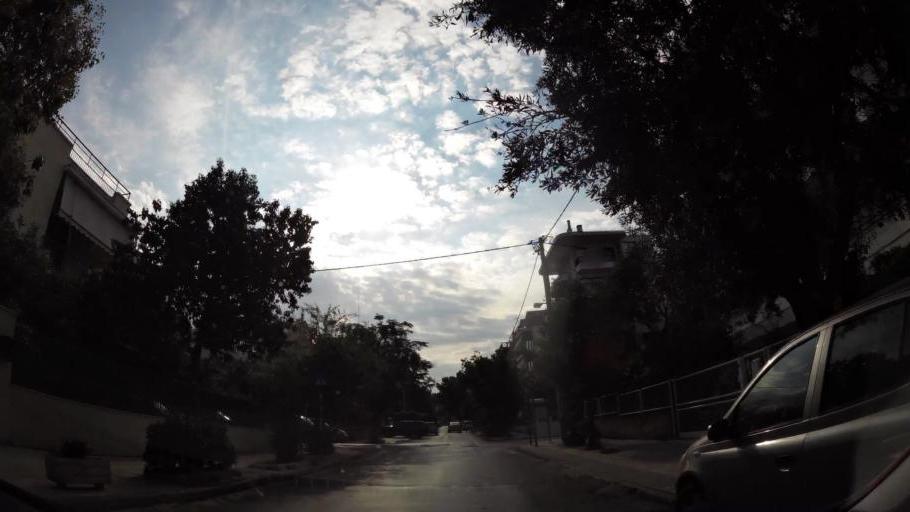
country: GR
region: Attica
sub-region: Nomarchia Athinas
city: Nea Smyrni
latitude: 37.9388
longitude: 23.7055
